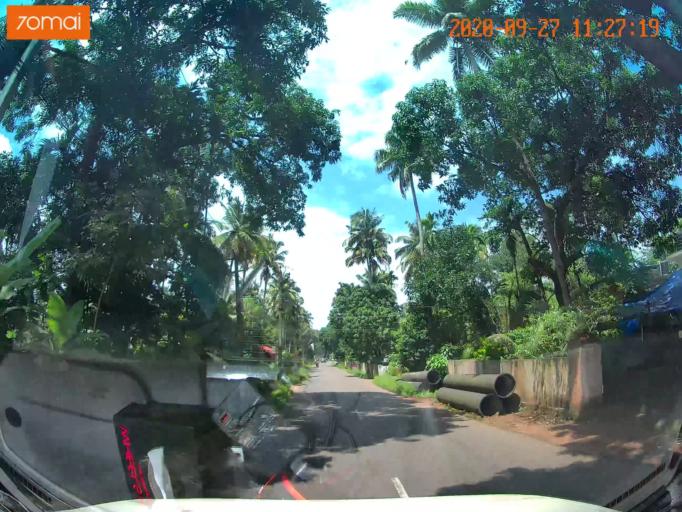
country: IN
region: Kerala
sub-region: Thrissur District
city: Thanniyam
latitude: 10.4168
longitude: 76.1478
